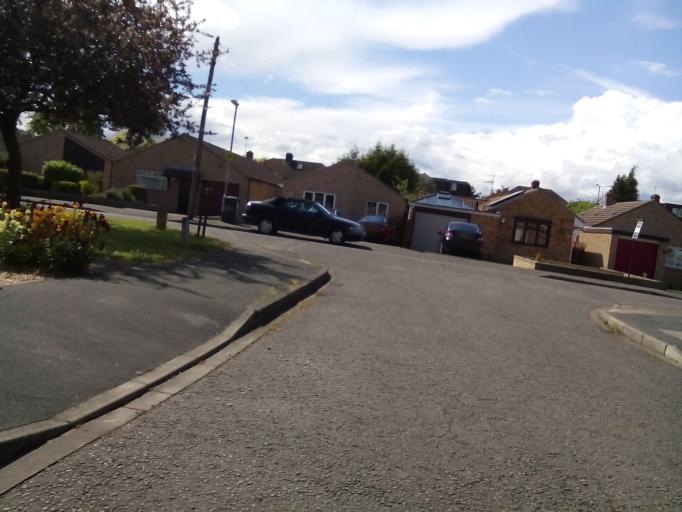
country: GB
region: England
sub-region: Cambridgeshire
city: Cambridge
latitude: 52.1932
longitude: 0.1567
